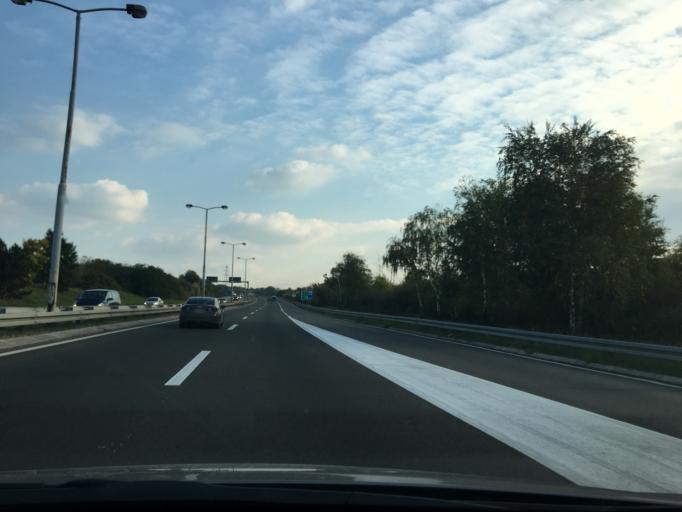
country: RS
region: Central Serbia
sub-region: Belgrade
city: Zvezdara
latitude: 44.7706
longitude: 20.5212
